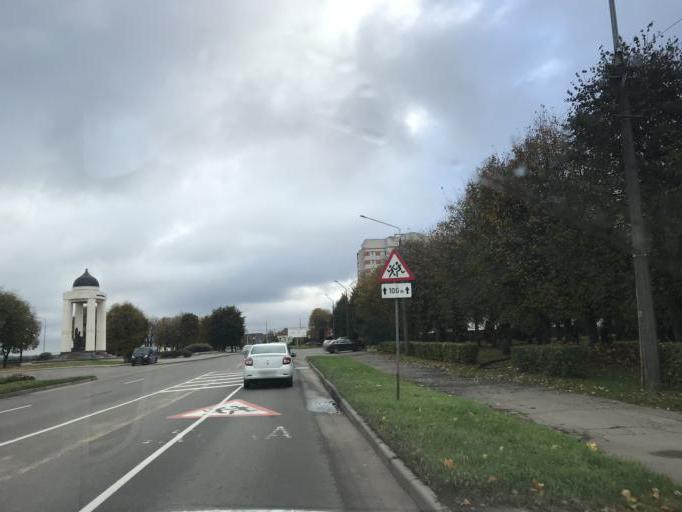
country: BY
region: Mogilev
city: Mahilyow
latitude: 53.8842
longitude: 30.3358
